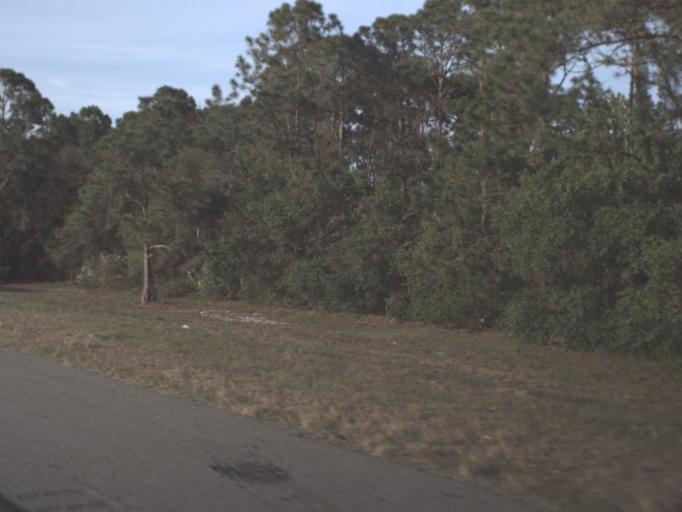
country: US
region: Florida
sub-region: Brevard County
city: Port Saint John
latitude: 28.4762
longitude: -80.8210
